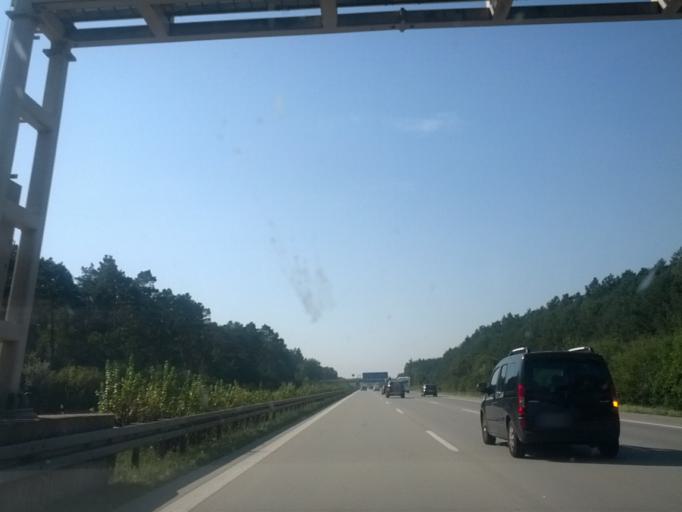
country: DE
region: Brandenburg
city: Erkner
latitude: 52.3415
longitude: 13.7544
